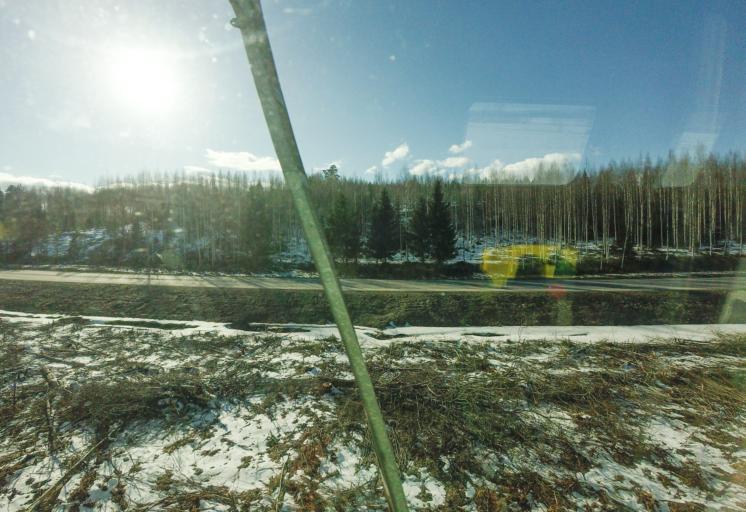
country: FI
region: South Karelia
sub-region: Imatra
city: Parikkala
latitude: 61.4878
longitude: 29.4850
